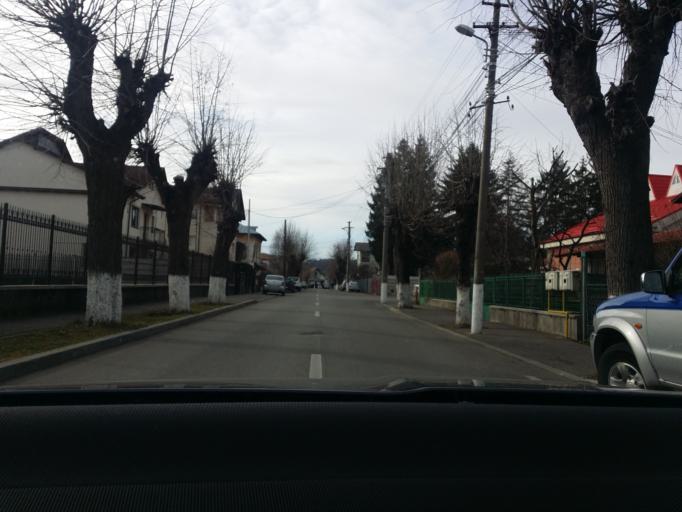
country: RO
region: Prahova
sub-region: Municipiul Campina
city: Campina
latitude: 45.1274
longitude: 25.7309
